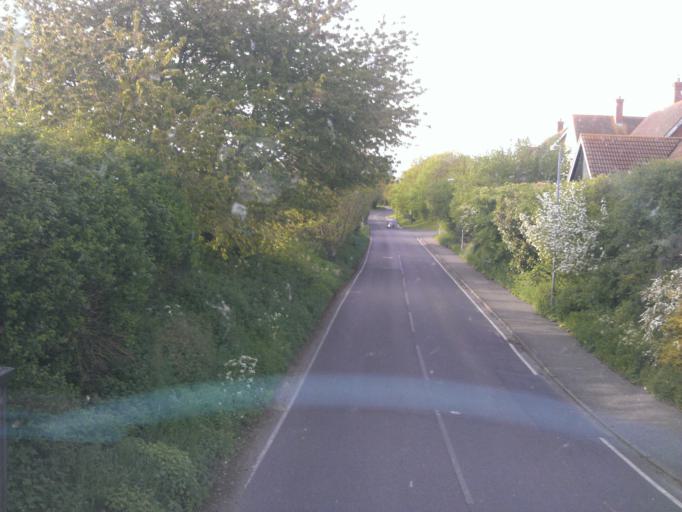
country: GB
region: England
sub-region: Essex
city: Coggeshall
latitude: 51.8781
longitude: 0.6920
